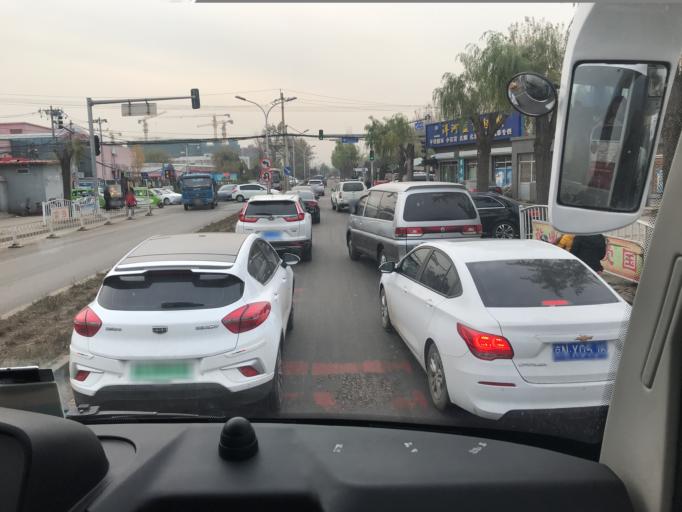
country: CN
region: Beijing
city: Sujiatuo
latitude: 40.0983
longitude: 116.2077
